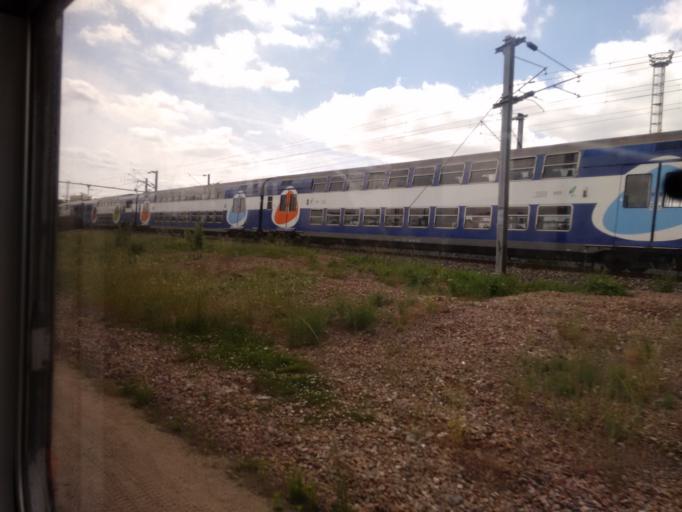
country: FR
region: Ile-de-France
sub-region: Paris
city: Saint-Ouen
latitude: 48.9032
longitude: 2.3540
